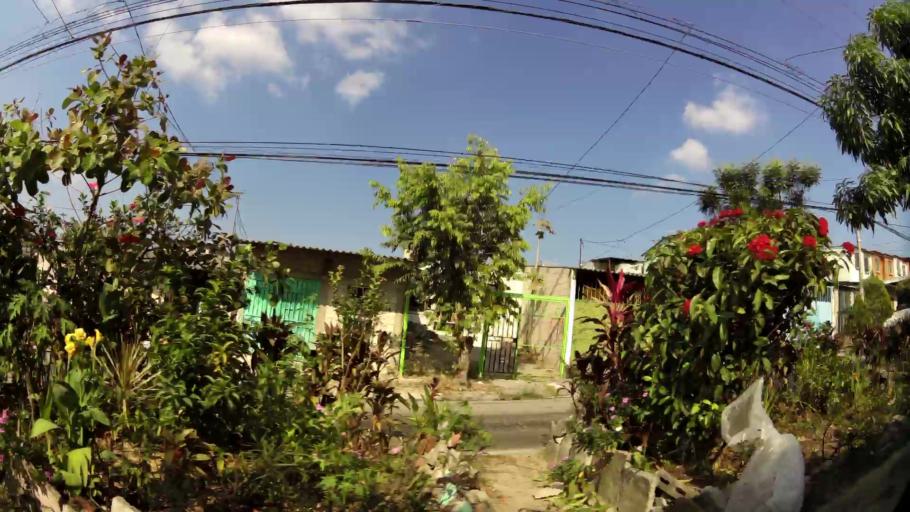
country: SV
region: San Salvador
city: Ilopango
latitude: 13.7240
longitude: -89.1080
